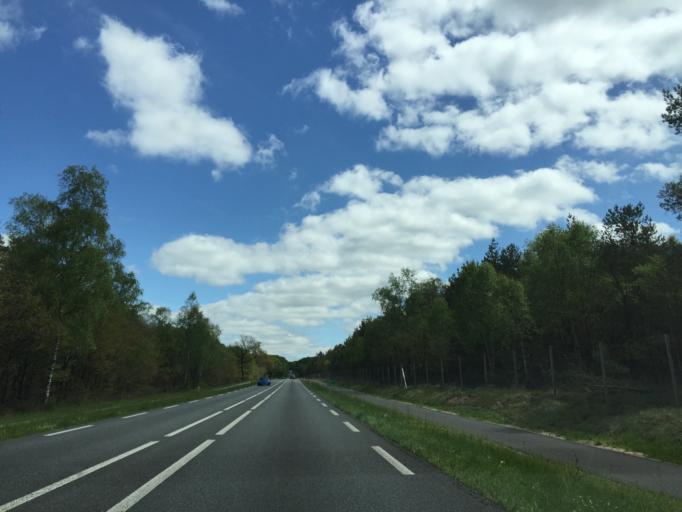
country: NL
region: Gelderland
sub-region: Gemeente Apeldoorn
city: Uddel
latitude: 52.2219
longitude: 5.8027
